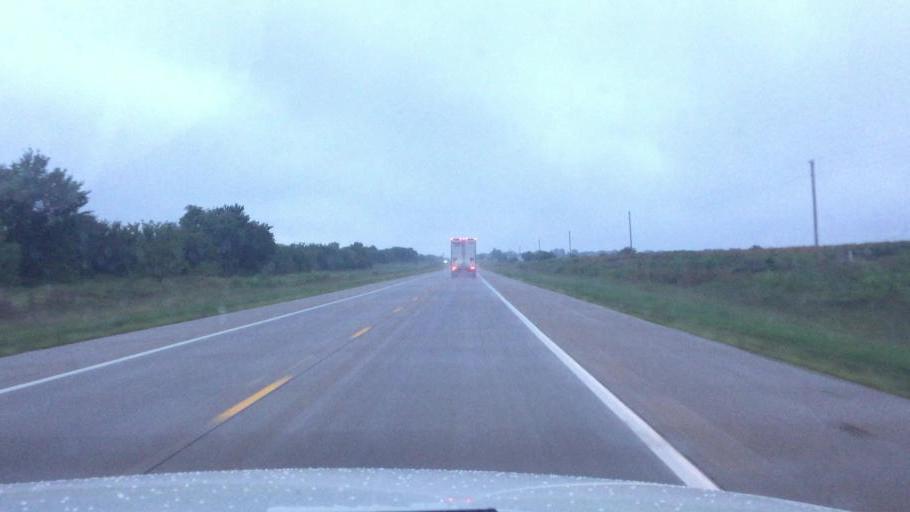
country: US
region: Kansas
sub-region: Neosho County
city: Chanute
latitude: 37.5109
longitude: -95.4709
